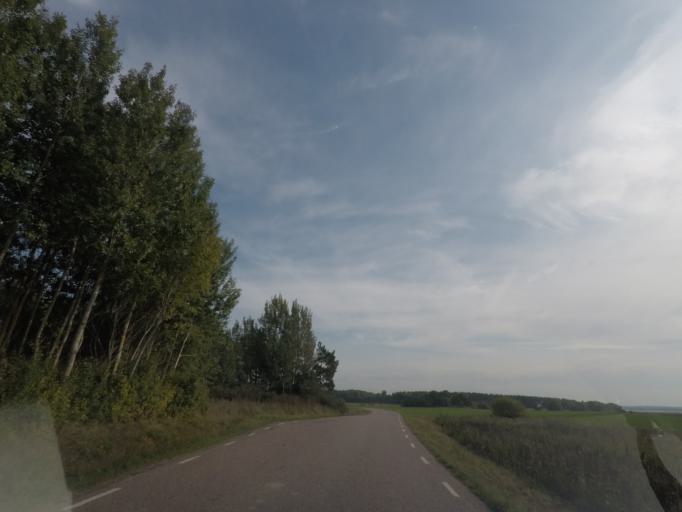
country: SE
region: Vaestmanland
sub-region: Kungsors Kommun
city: Kungsoer
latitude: 59.4933
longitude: 16.1550
